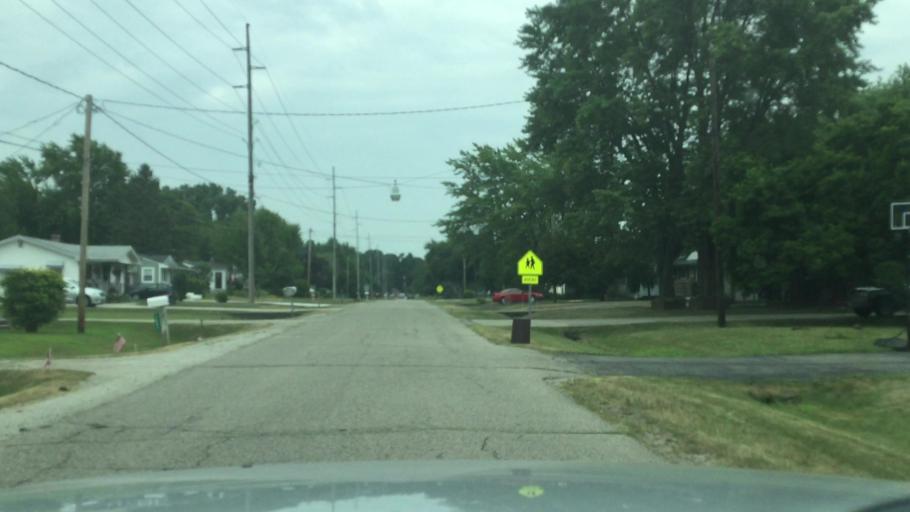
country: US
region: Michigan
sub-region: Genesee County
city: Flint
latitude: 42.9719
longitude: -83.7029
